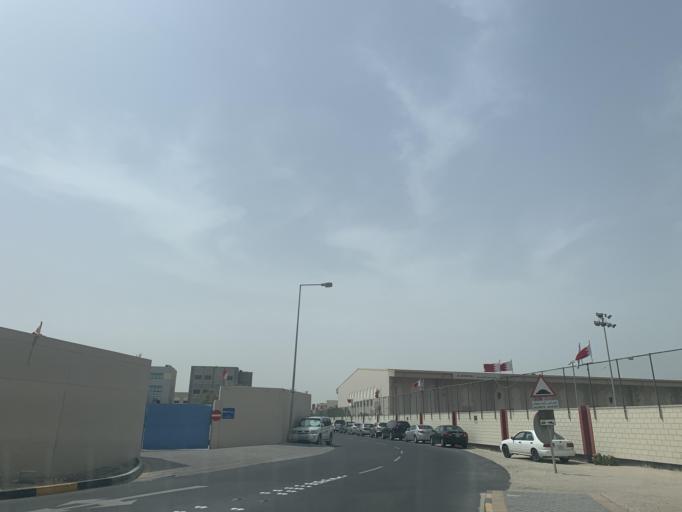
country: BH
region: Northern
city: Madinat `Isa
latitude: 26.1618
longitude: 50.5511
